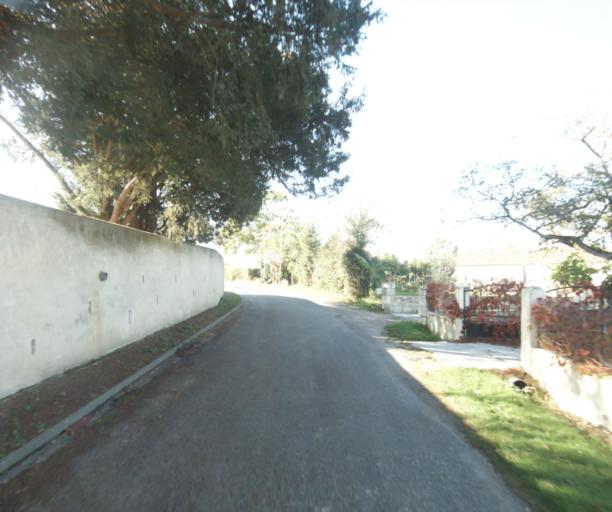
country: FR
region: Midi-Pyrenees
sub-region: Departement du Gers
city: Eauze
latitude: 43.7967
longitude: 0.1447
